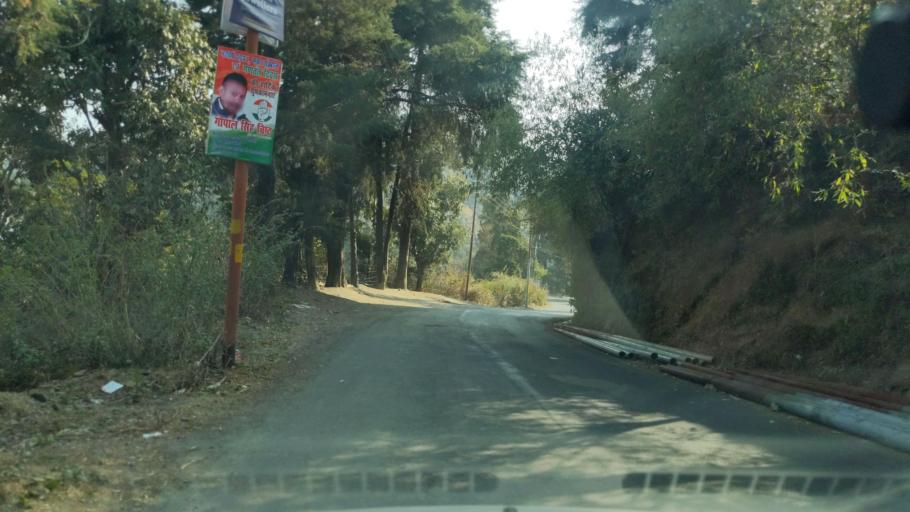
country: IN
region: Uttarakhand
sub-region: Naini Tal
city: Bhowali
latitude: 29.3908
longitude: 79.5314
